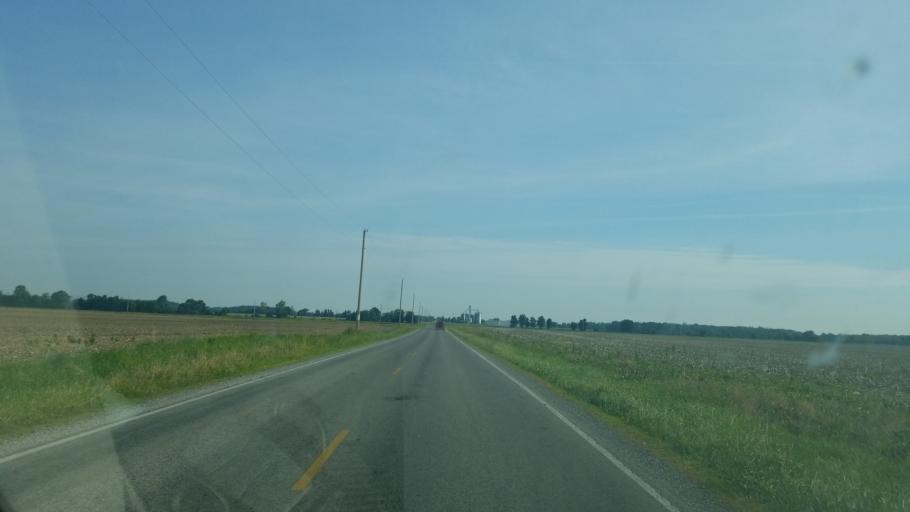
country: US
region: Ohio
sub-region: Hancock County
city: Arlington
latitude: 40.9656
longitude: -83.6985
